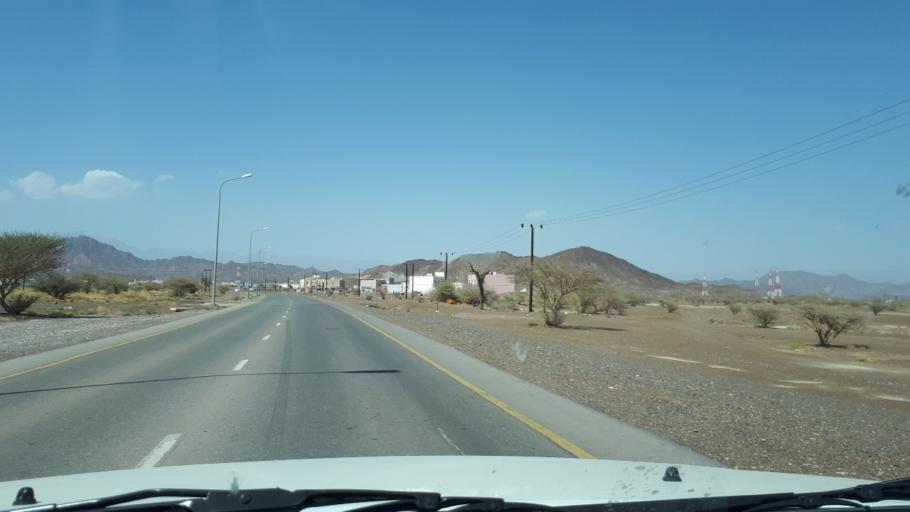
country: OM
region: Muhafazat ad Dakhiliyah
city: Bahla'
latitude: 22.9187
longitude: 57.2541
